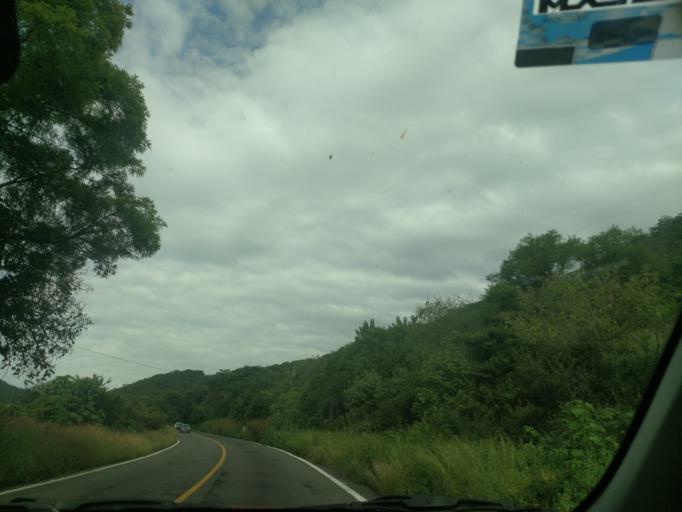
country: MX
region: Jalisco
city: Ameca
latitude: 20.5283
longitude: -104.2133
